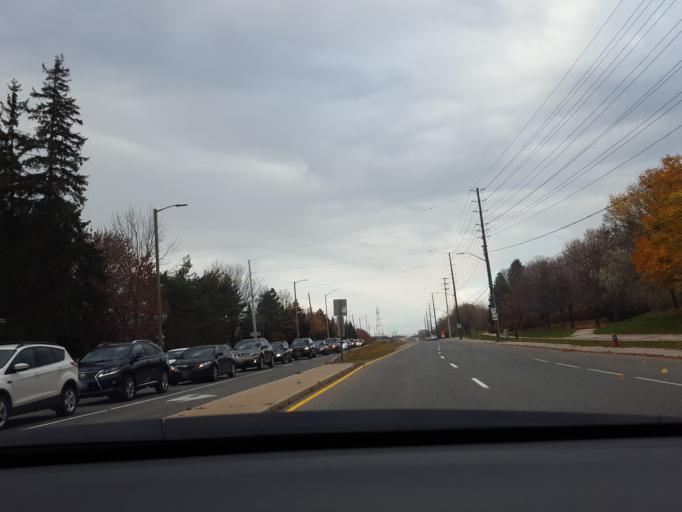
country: CA
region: Ontario
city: Mississauga
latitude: 43.5366
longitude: -79.7005
